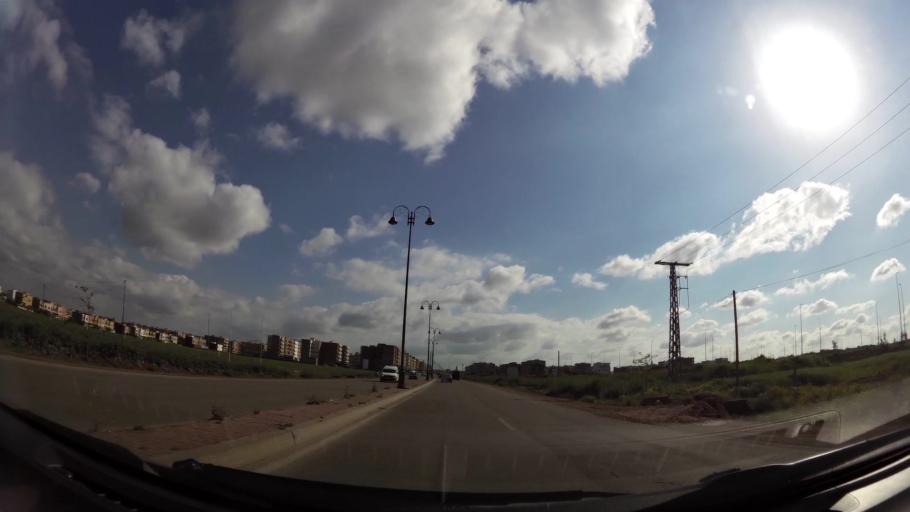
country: MA
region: Chaouia-Ouardigha
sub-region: Settat Province
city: Berrechid
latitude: 33.2817
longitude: -7.5797
